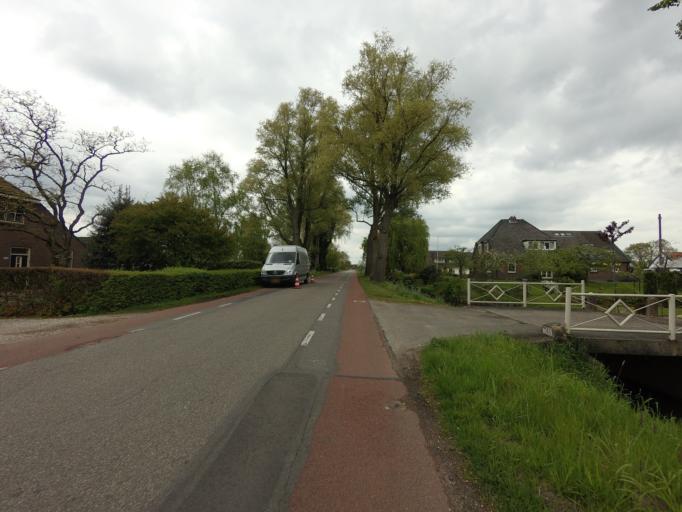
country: NL
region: North Holland
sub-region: Gemeente Wijdemeren
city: Nieuw-Loosdrecht
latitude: 52.1579
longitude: 5.1076
